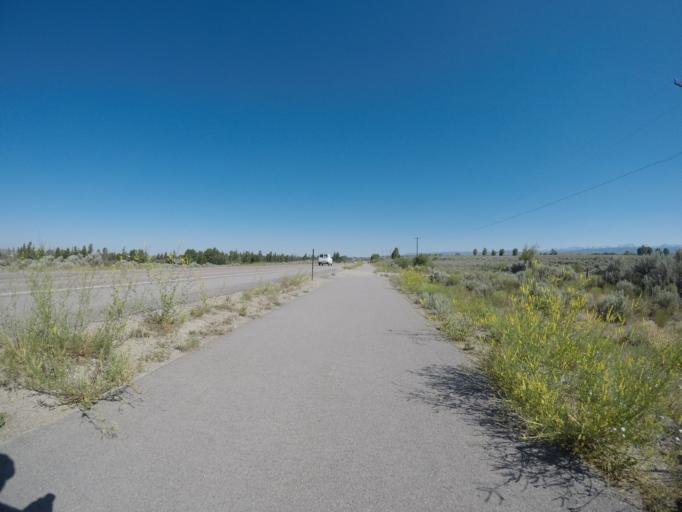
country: US
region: Wyoming
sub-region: Sublette County
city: Pinedale
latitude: 42.8459
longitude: -109.8479
